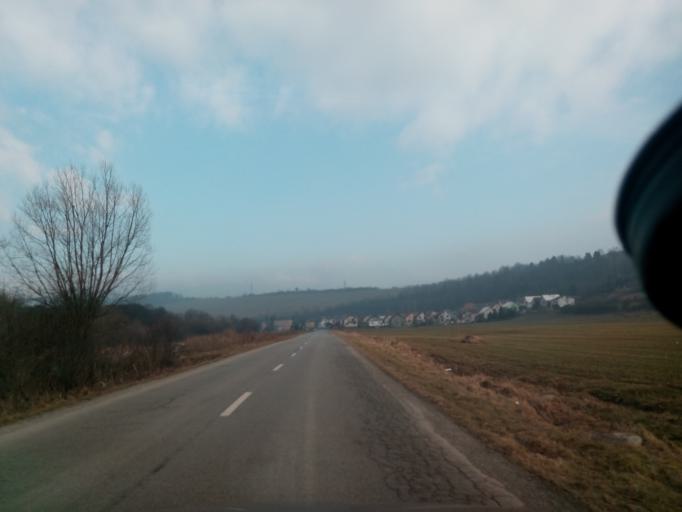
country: SK
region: Presovsky
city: Lipany
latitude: 49.1681
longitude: 20.8698
